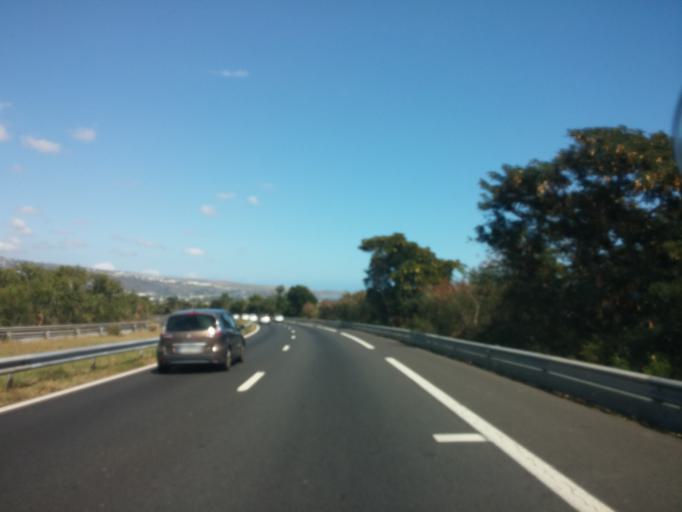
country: RE
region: Reunion
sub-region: Reunion
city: Le Port
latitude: -20.9645
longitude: 55.3001
